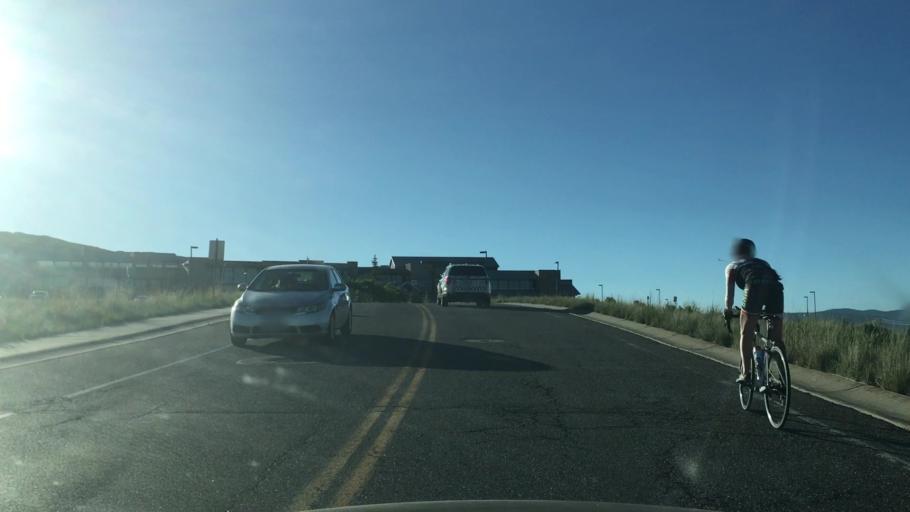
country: US
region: Utah
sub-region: Summit County
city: Park City
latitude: 40.6868
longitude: -111.4667
